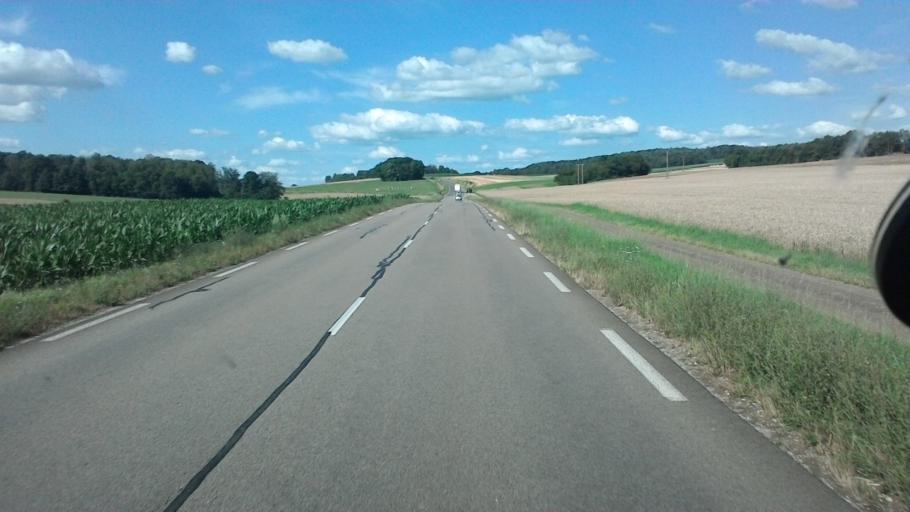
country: FR
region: Franche-Comte
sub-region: Departement de la Haute-Saone
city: Echenoz-la-Meline
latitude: 47.5468
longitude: 6.0574
